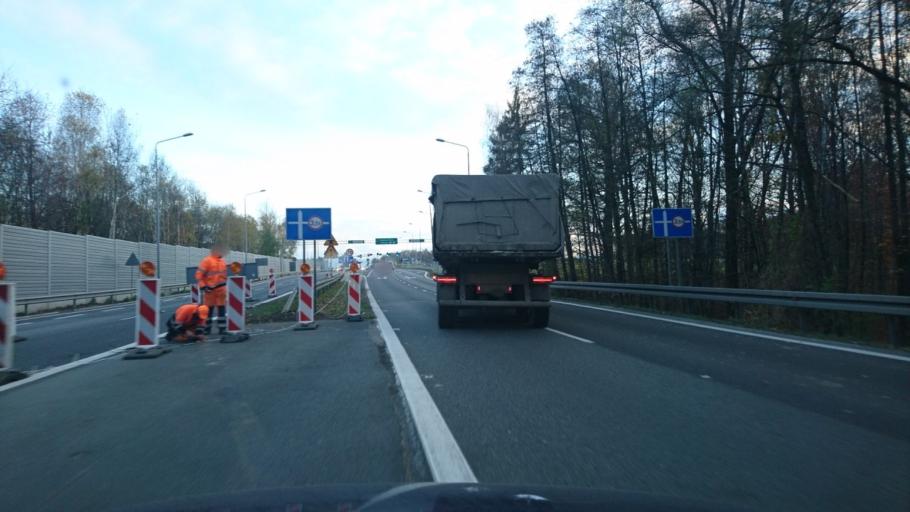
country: PL
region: Silesian Voivodeship
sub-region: Powiat bielski
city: Mazancowice
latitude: 49.8732
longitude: 19.0029
